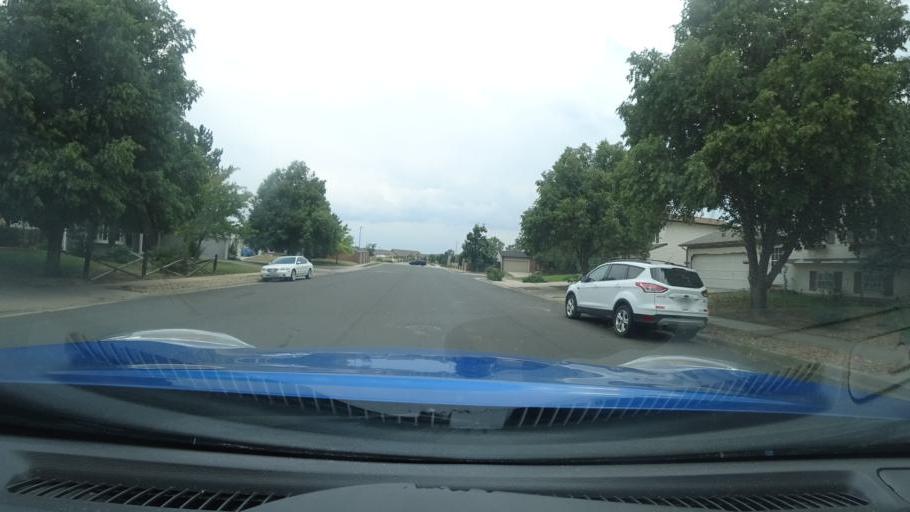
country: US
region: Colorado
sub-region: Adams County
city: Aurora
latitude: 39.6830
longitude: -104.7603
